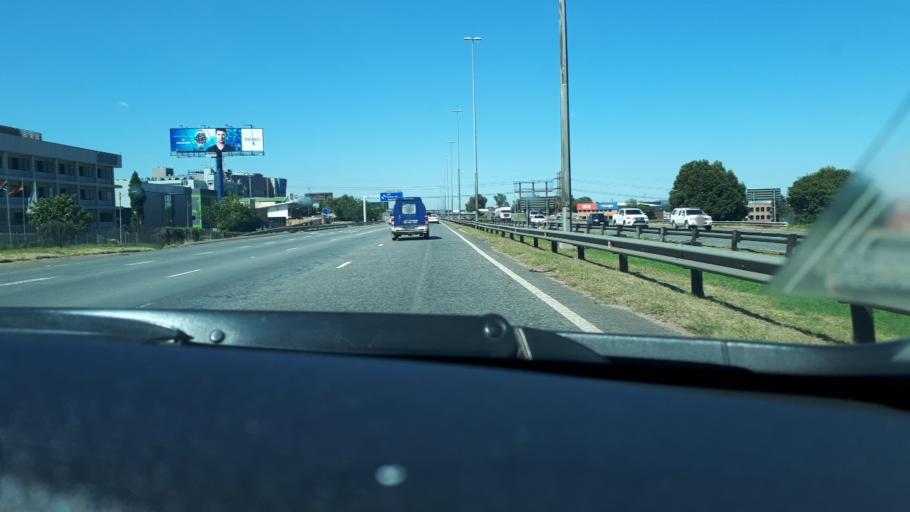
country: ZA
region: Gauteng
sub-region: City of Johannesburg Metropolitan Municipality
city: Modderfontein
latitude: -26.1348
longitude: 28.1999
